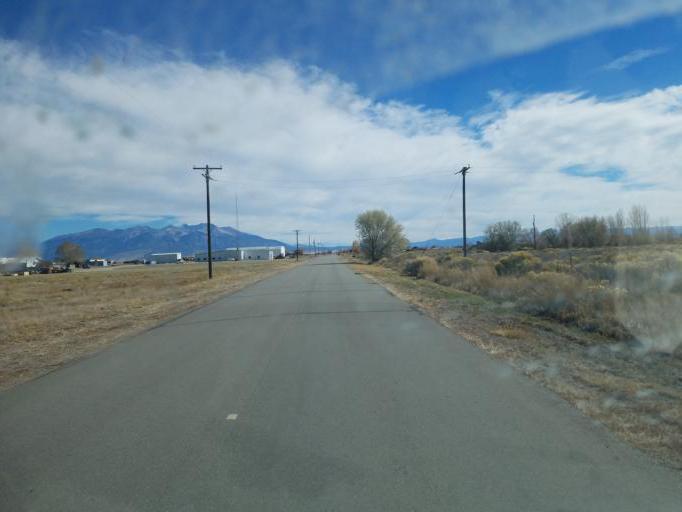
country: US
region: Colorado
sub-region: Alamosa County
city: Alamosa East
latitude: 37.5027
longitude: -105.8205
